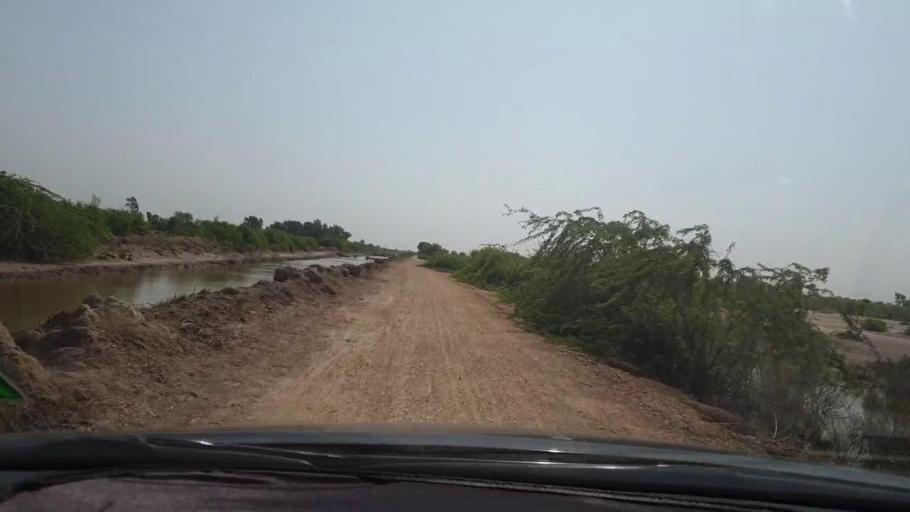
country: PK
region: Sindh
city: Tando Bago
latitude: 24.7963
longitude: 69.1073
